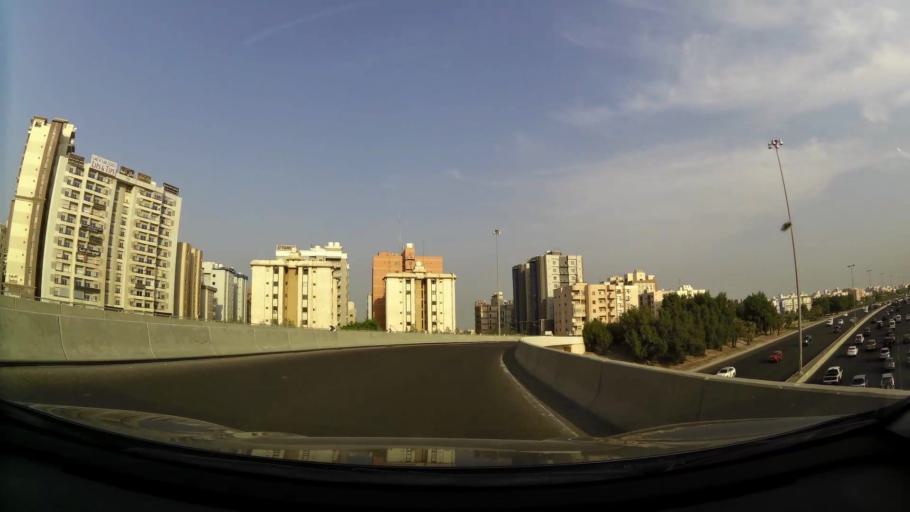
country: KW
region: Muhafazat Hawalli
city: Hawalli
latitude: 29.3185
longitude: 48.0155
